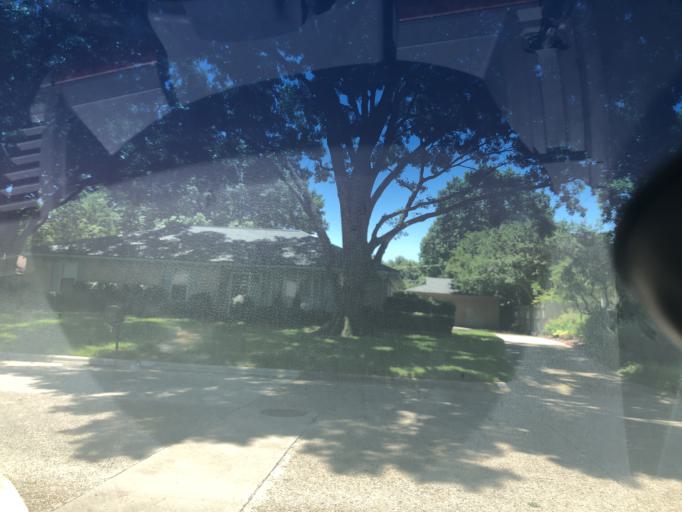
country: US
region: Texas
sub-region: Dallas County
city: Grand Prairie
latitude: 32.7760
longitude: -97.0384
